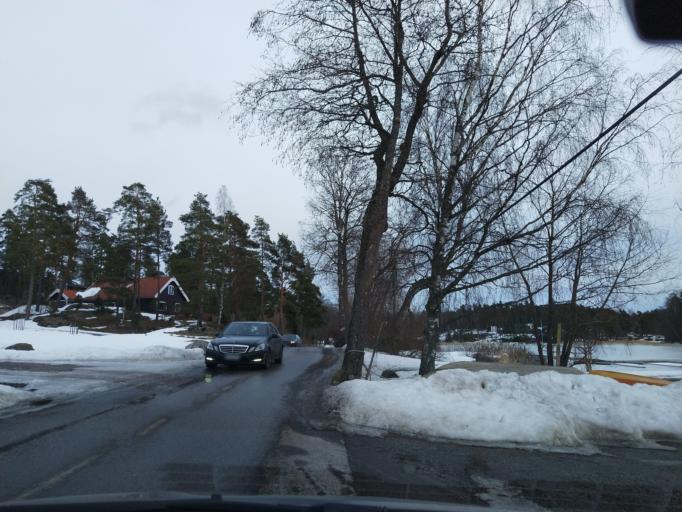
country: FI
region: Uusimaa
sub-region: Helsinki
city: Sibbo
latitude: 60.2567
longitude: 25.3028
